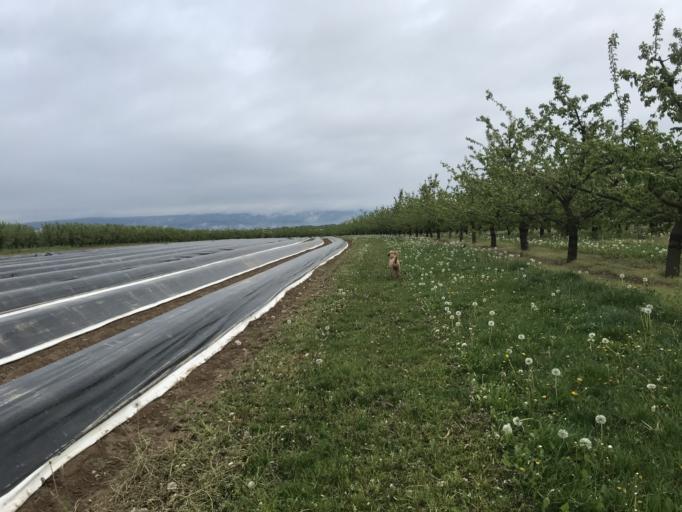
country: DE
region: Rheinland-Pfalz
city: Budenheim
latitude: 49.9739
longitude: 8.1635
